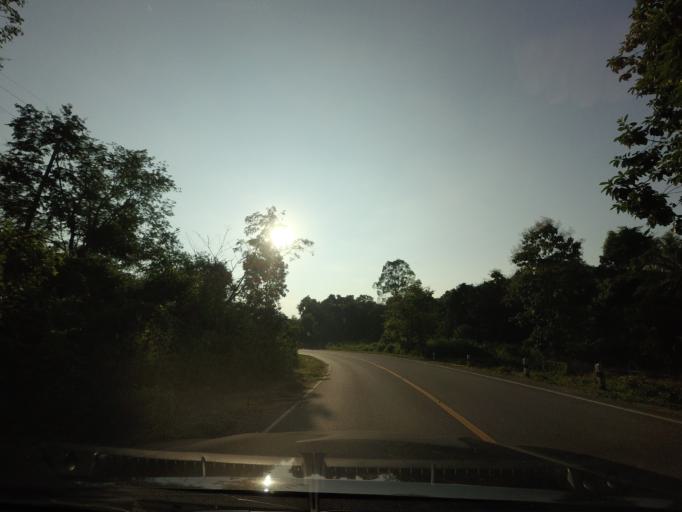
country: TH
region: Nan
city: Na Noi
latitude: 18.3359
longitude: 100.7777
